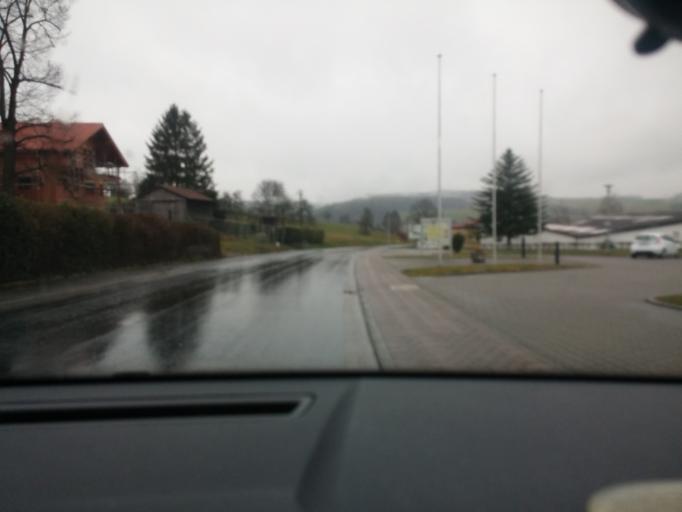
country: DE
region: Hesse
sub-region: Regierungsbezirk Darmstadt
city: Bad Konig
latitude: 49.7327
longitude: 8.9571
